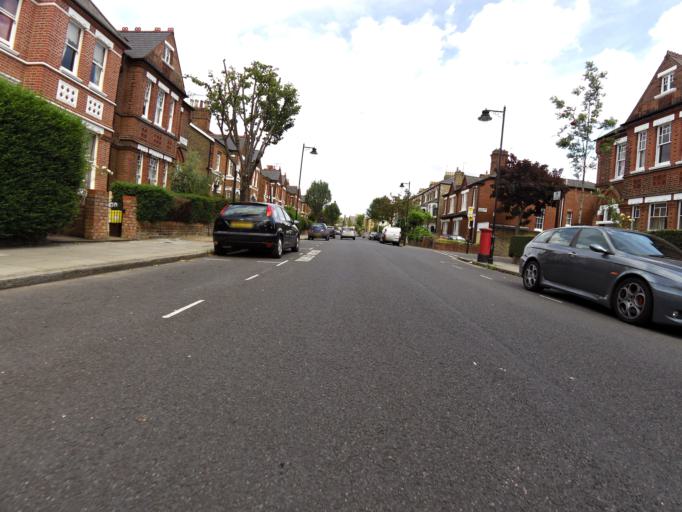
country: GB
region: England
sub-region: Greater London
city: Holloway
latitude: 51.5595
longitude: -0.1302
